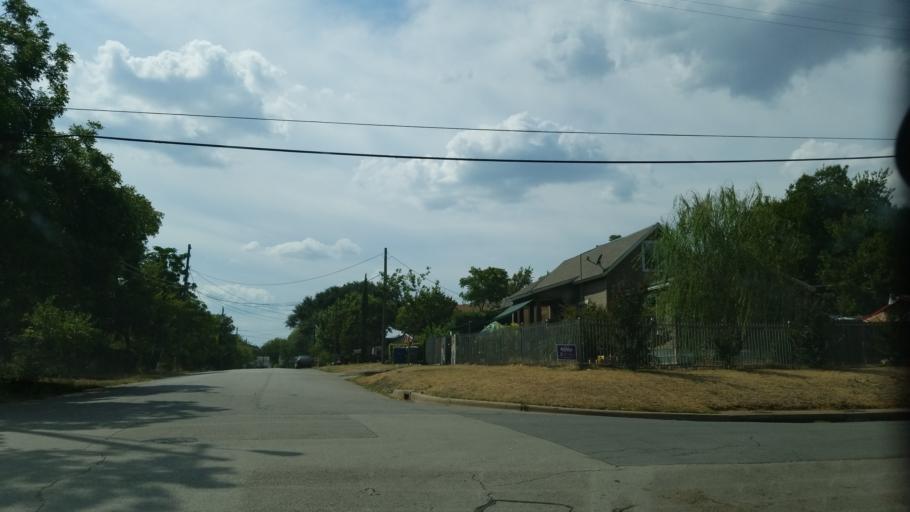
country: US
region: Texas
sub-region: Dallas County
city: Dallas
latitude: 32.7674
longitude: -96.8418
